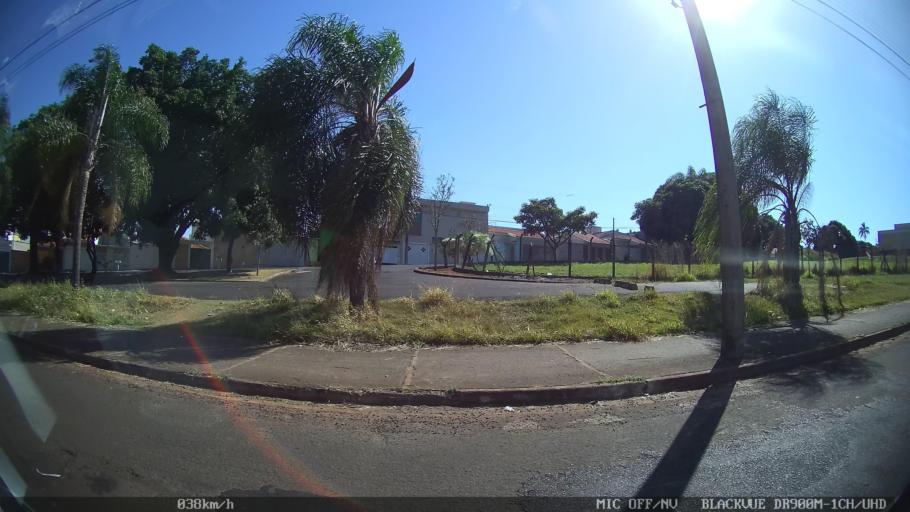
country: BR
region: Sao Paulo
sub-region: Batatais
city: Batatais
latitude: -20.8872
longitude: -47.5753
